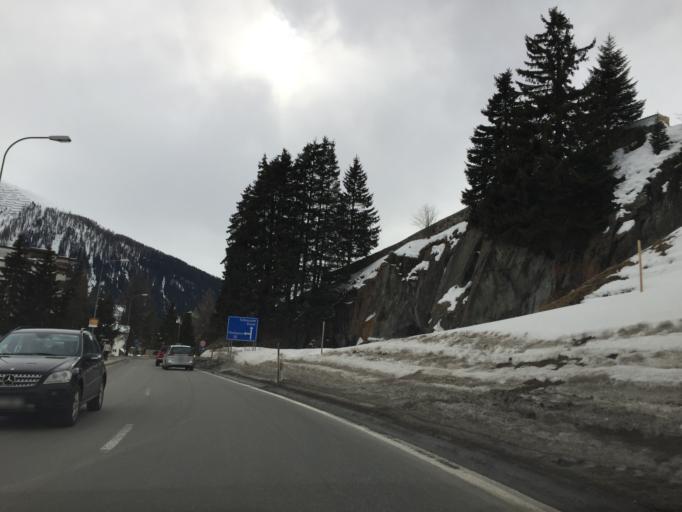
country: CH
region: Grisons
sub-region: Praettigau/Davos District
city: Davos
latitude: 46.8135
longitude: 9.8456
